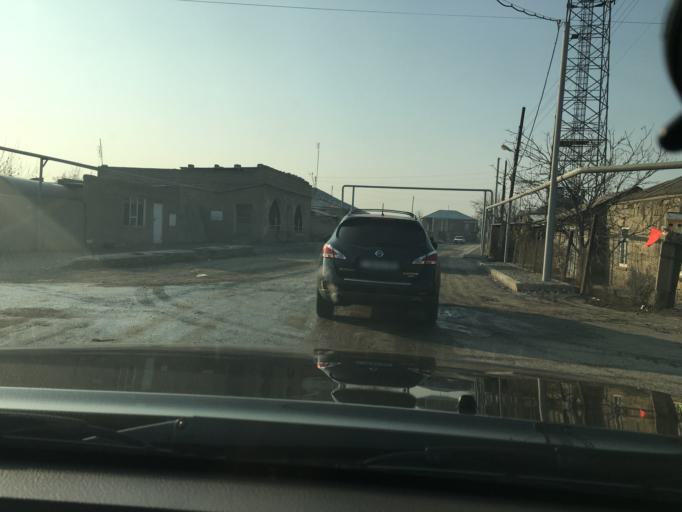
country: AM
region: Armavir
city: Janfida
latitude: 40.0455
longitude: 44.0295
